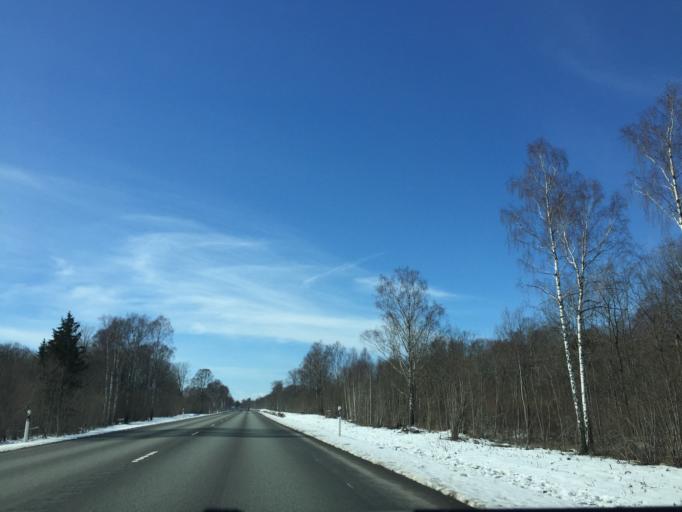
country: EE
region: Laeaene
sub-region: Lihula vald
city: Lihula
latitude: 58.6180
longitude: 23.6185
